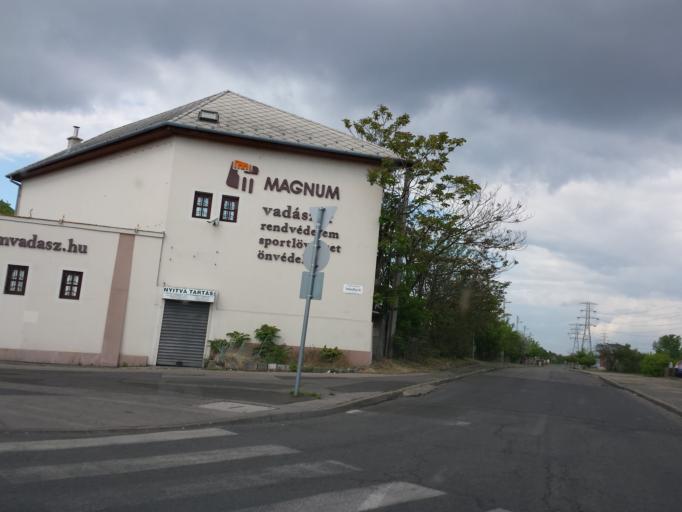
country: HU
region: Budapest
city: Budapest XX. keruelet
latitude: 47.4437
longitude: 19.0932
